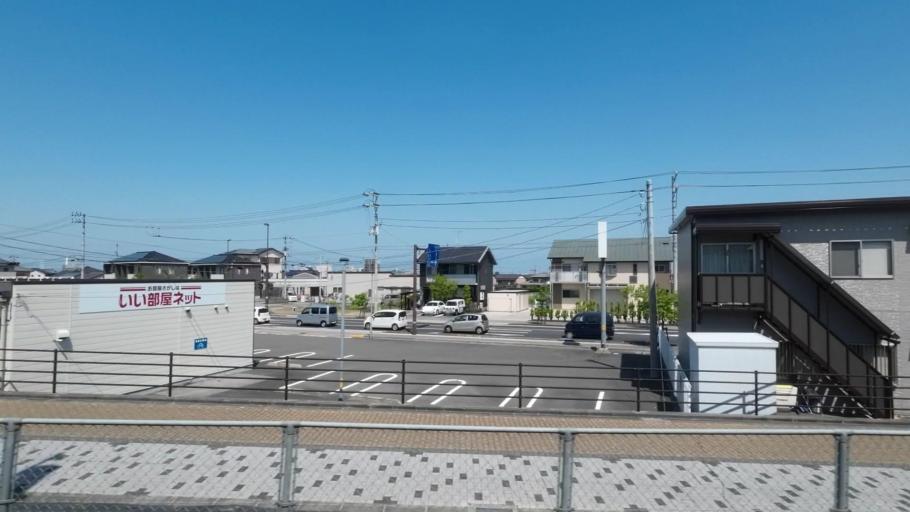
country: JP
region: Ehime
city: Niihama
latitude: 33.9508
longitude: 133.2977
